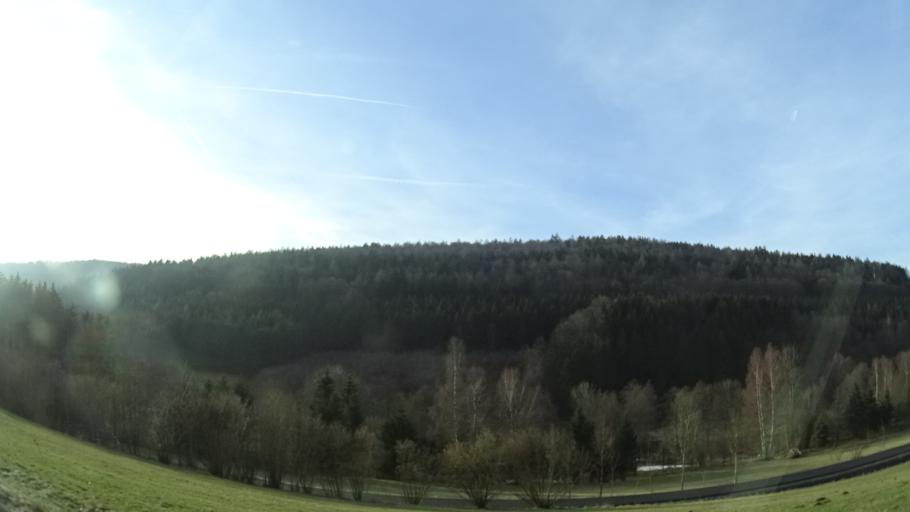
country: DE
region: Bavaria
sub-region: Regierungsbezirk Unterfranken
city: Riedenberg
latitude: 50.3342
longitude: 9.8771
